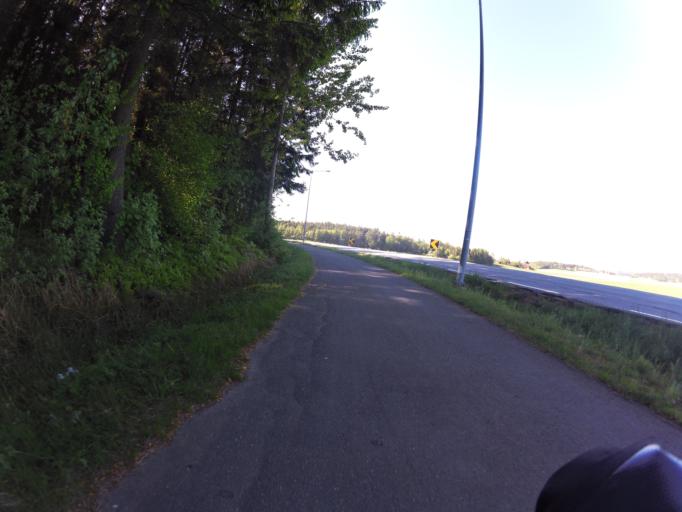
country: NO
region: Ostfold
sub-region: Sarpsborg
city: Sarpsborg
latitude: 59.2277
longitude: 11.0353
